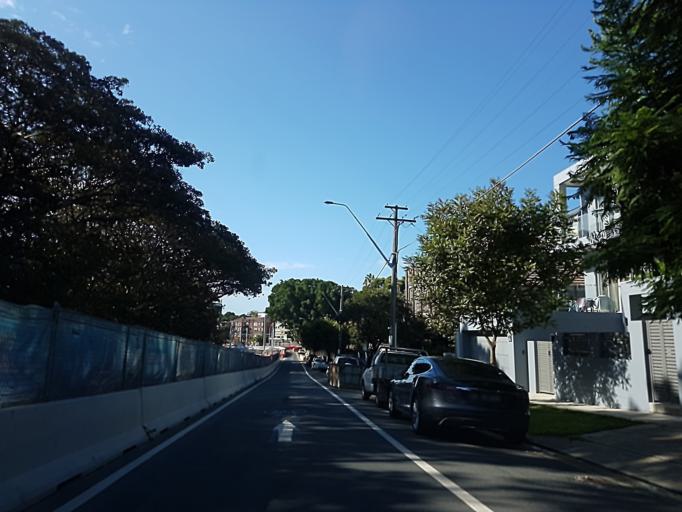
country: AU
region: New South Wales
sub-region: Randwick
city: Kingsford
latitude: -33.9133
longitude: 151.2354
